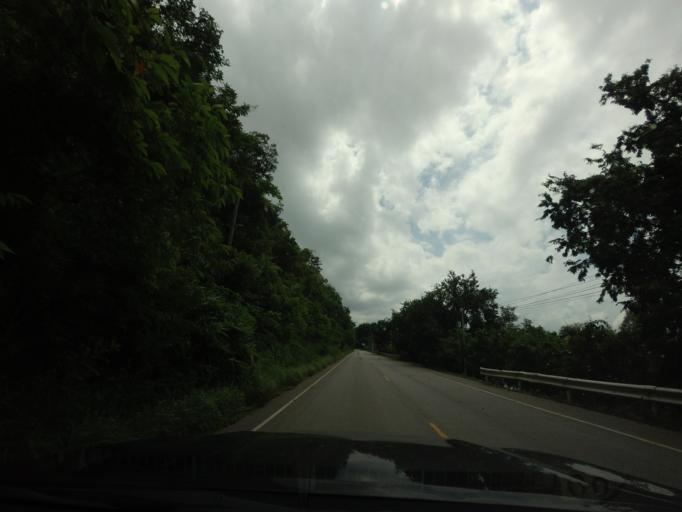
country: TH
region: Loei
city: Pak Chom
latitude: 18.0591
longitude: 101.7773
